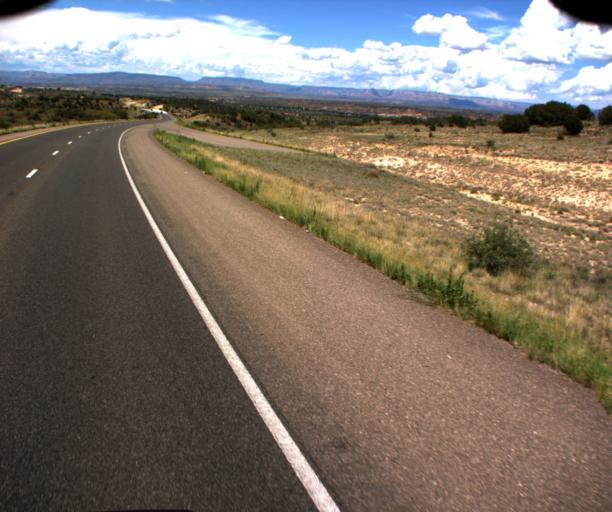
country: US
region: Arizona
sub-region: Yavapai County
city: Verde Village
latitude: 34.6648
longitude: -111.9675
